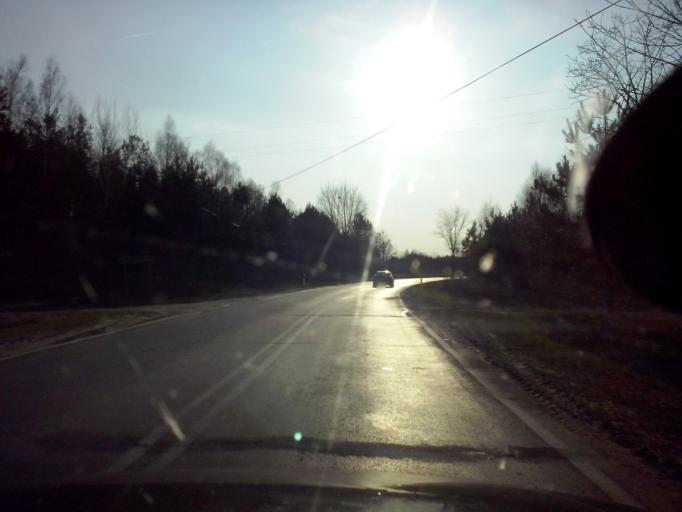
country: PL
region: Lublin Voivodeship
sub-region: Powiat janowski
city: Potok Wielki
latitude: 50.7528
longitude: 22.1761
